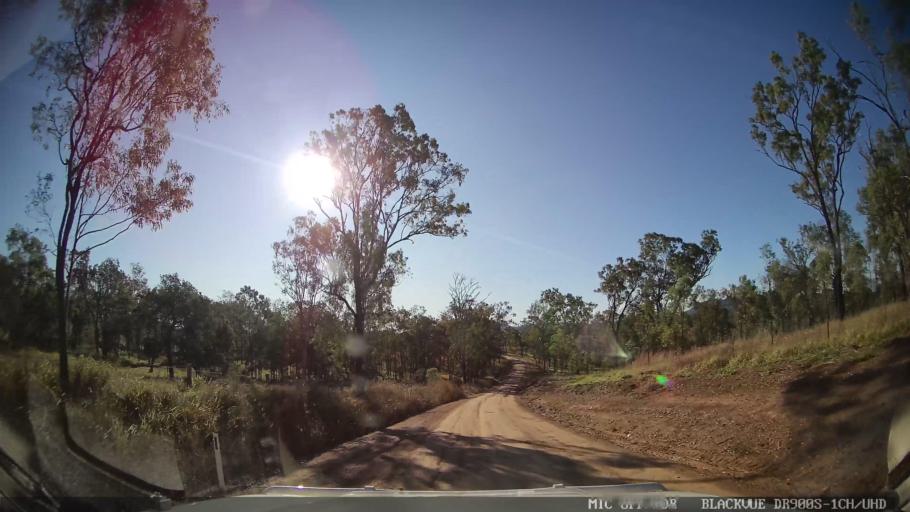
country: AU
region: Queensland
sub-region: Bundaberg
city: Sharon
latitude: -24.7894
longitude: 151.6077
